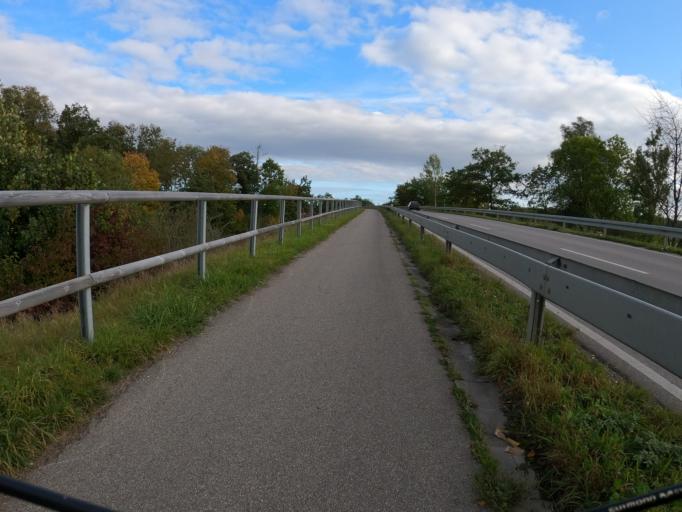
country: DE
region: Bavaria
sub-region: Swabia
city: Holzheim
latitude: 48.4029
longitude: 10.0897
